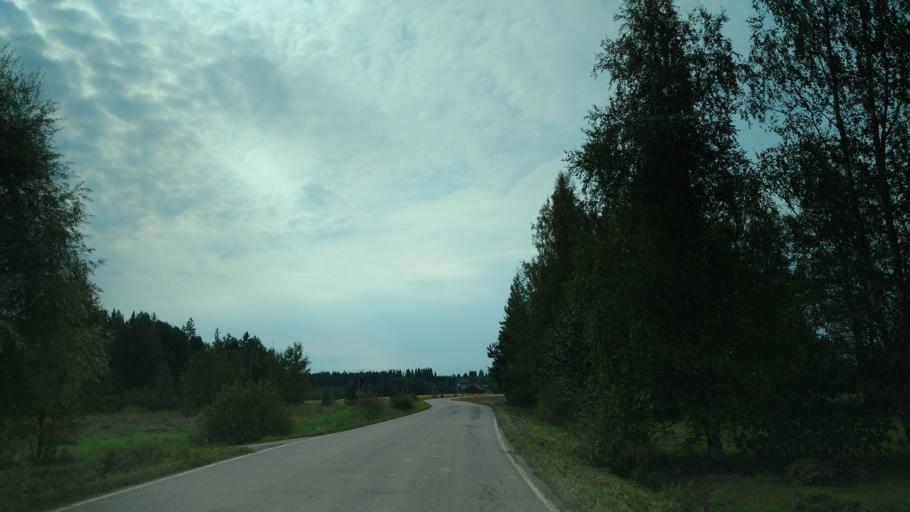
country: FI
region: Varsinais-Suomi
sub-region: Loimaa
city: Koski Tl
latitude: 60.7032
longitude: 23.1665
